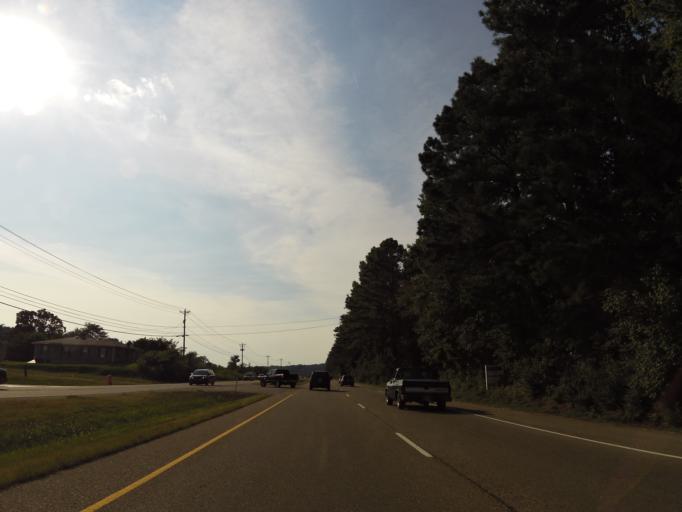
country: US
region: Tennessee
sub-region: Loudon County
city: Lenoir City
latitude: 35.8326
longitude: -84.2857
